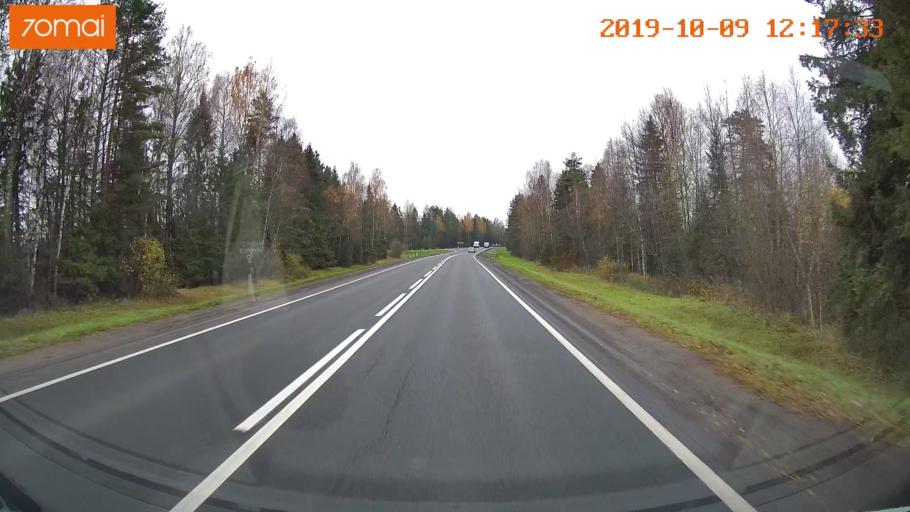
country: RU
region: Jaroslavl
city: Prechistoye
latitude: 58.4546
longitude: 40.3216
